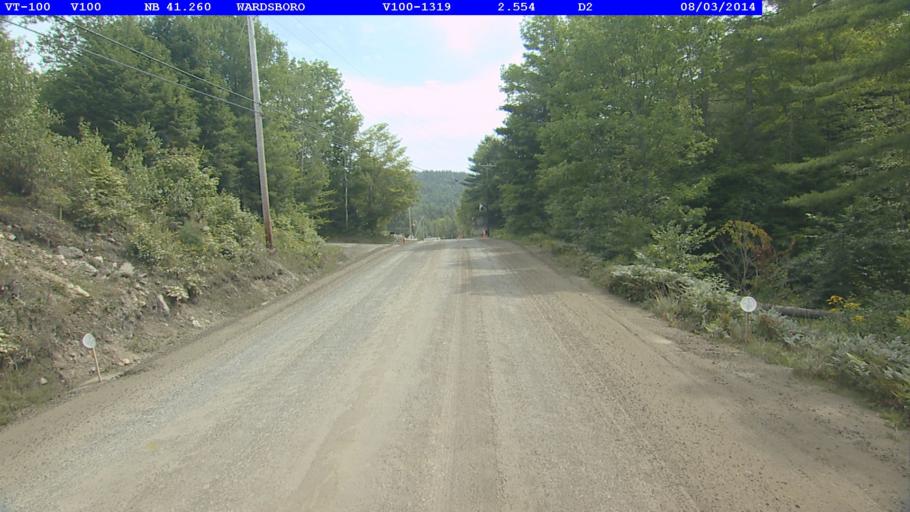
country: US
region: Vermont
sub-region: Windham County
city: Dover
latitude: 43.0326
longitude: -72.8486
